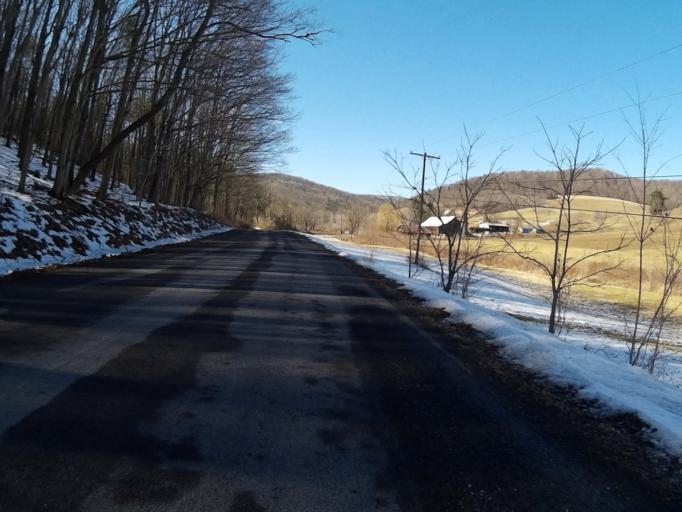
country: US
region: Pennsylvania
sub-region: Centre County
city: Stormstown
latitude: 40.8345
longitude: -78.0136
